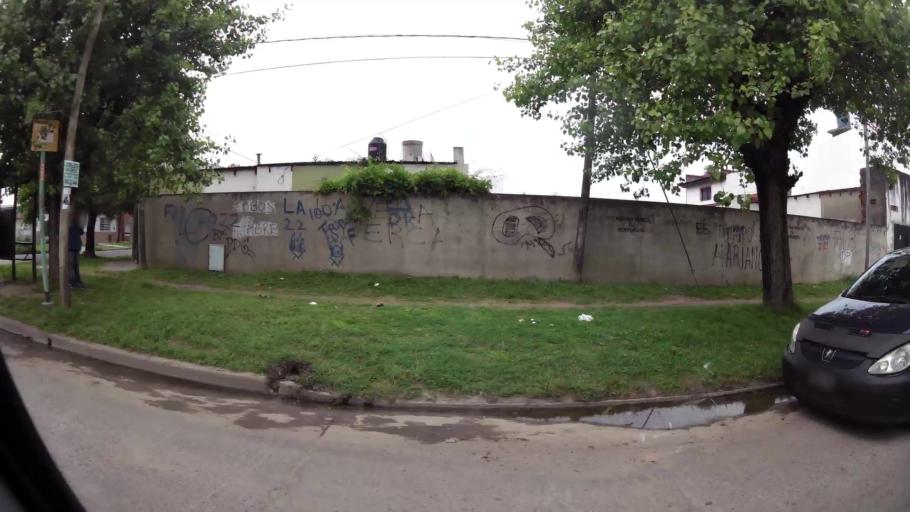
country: AR
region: Buenos Aires
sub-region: Partido de La Plata
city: La Plata
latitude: -34.9144
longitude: -57.9964
